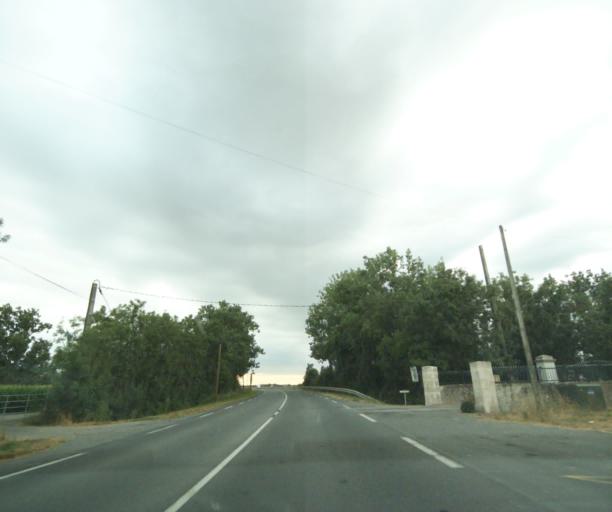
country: FR
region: Pays de la Loire
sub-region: Departement de la Vendee
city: Chaille-les-Marais
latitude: 46.4121
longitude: -1.0425
